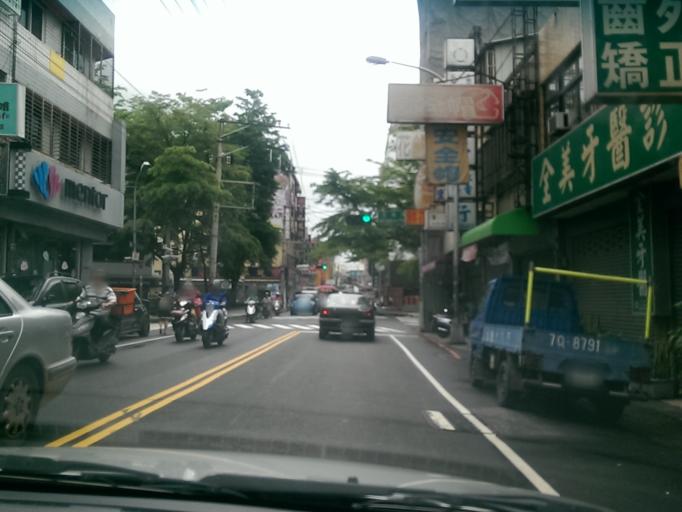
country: TW
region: Taiwan
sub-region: Taichung City
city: Taichung
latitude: 24.1778
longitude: 120.6426
